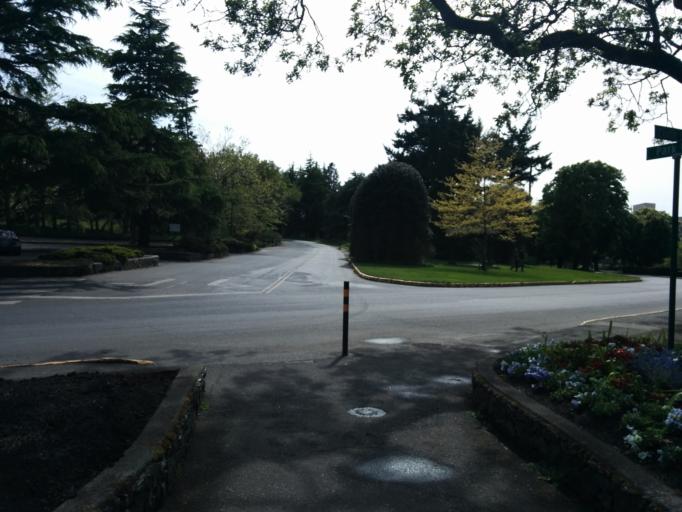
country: CA
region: British Columbia
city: Victoria
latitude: 48.4128
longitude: -123.3654
